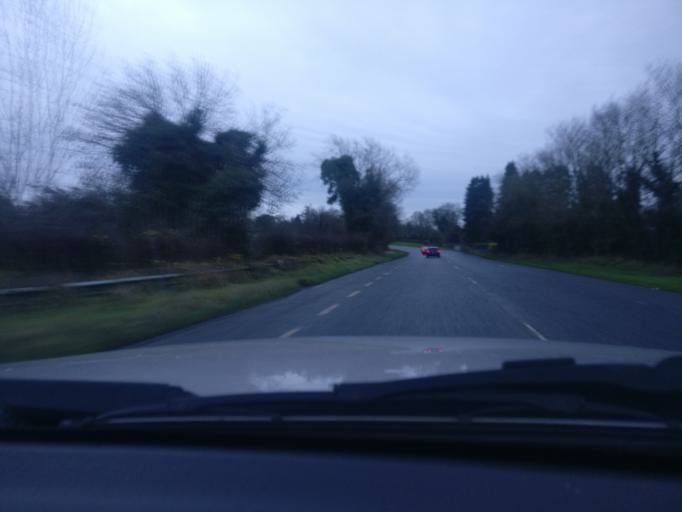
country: IE
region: Leinster
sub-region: An Mhi
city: Kells
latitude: 53.6970
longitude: -6.7889
